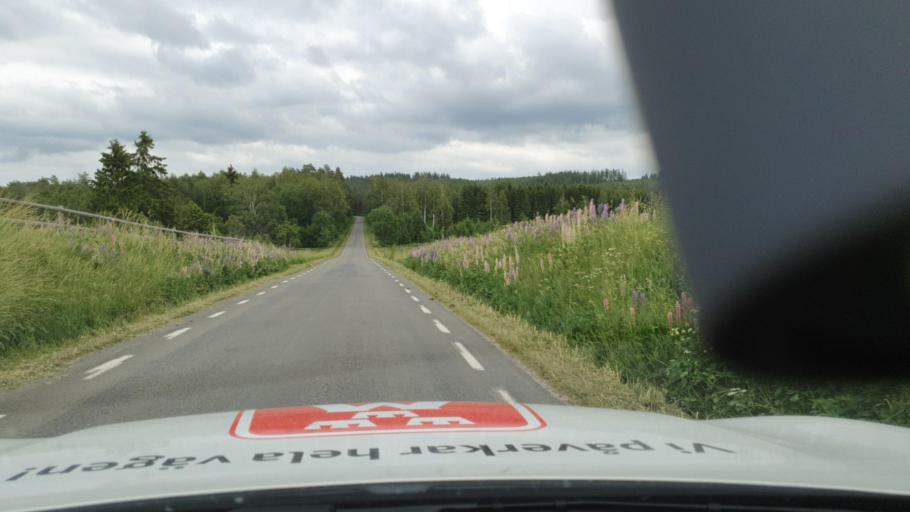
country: SE
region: Vaestra Goetaland
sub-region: Tidaholms Kommun
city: Olofstorp
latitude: 58.1896
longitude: 14.0779
